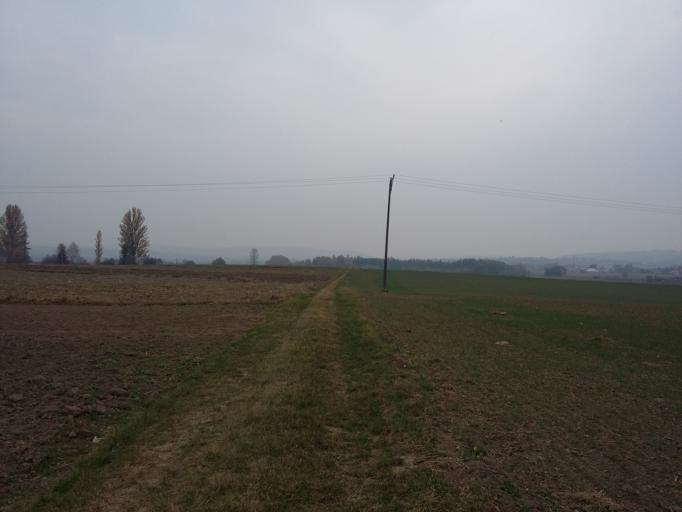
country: PL
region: Subcarpathian Voivodeship
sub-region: Powiat jasielski
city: Tarnowiec
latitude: 49.7324
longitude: 21.5666
